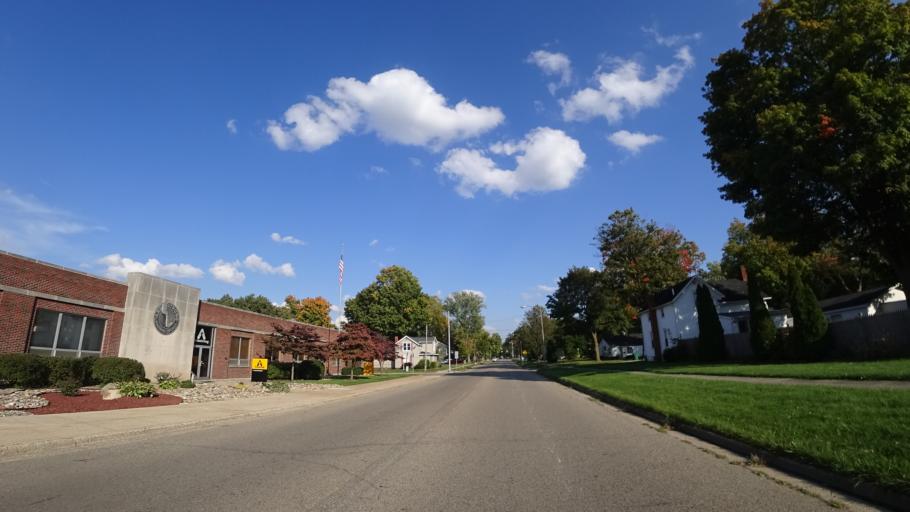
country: US
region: Michigan
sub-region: Saint Joseph County
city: Three Rivers
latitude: 41.9547
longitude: -85.6381
